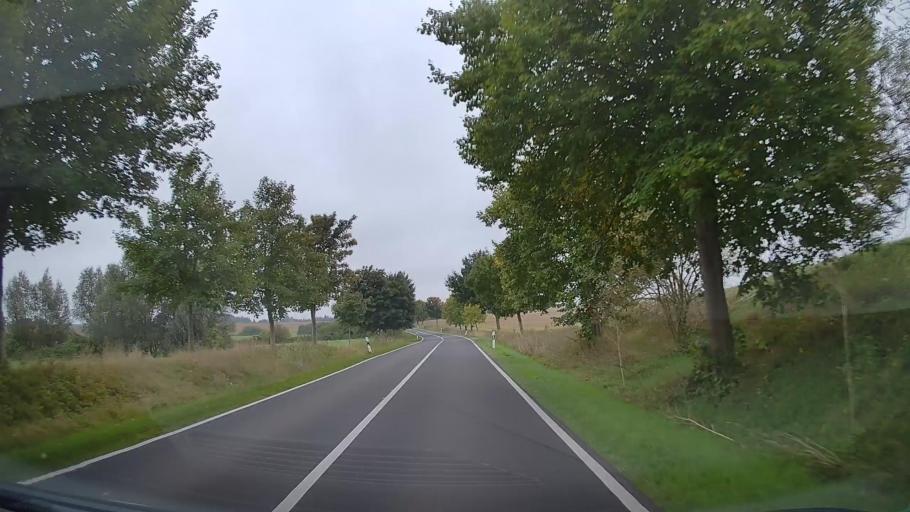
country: DE
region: Mecklenburg-Vorpommern
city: Schwaan
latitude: 53.9024
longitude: 12.1948
